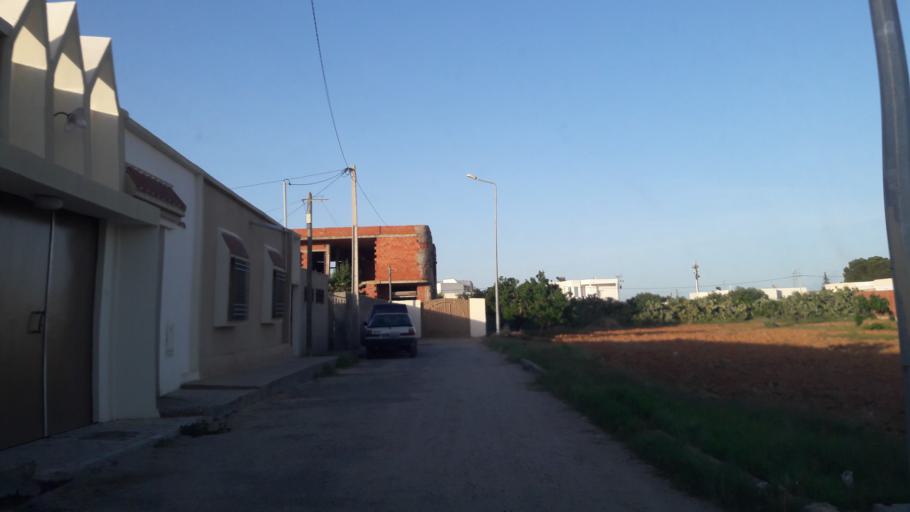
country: TN
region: Safaqis
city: Al Qarmadah
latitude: 34.8203
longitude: 10.7440
